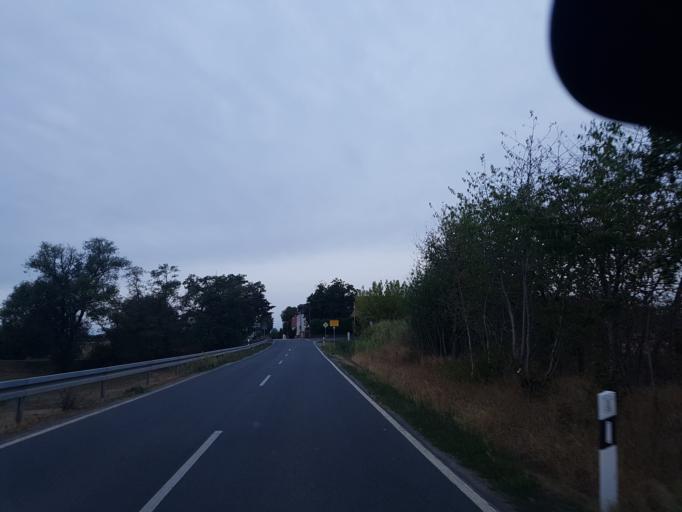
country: DE
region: Saxony
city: Belgern
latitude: 51.4928
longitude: 13.1880
